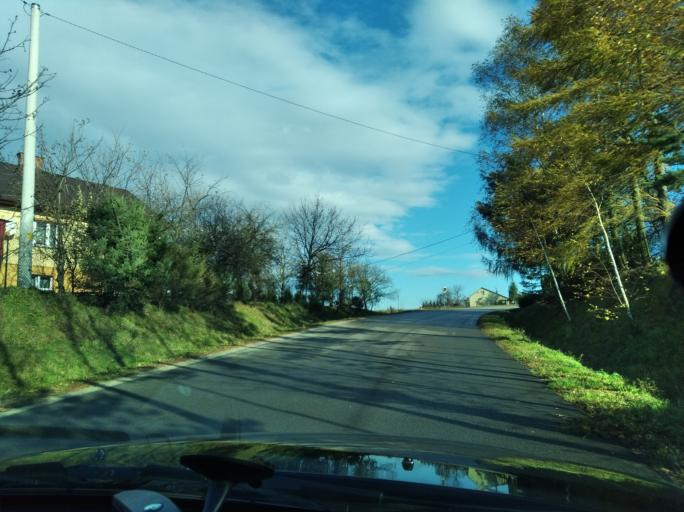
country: PL
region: Subcarpathian Voivodeship
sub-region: Powiat ropczycko-sedziszowski
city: Niedzwiada
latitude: 50.0076
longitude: 21.4733
